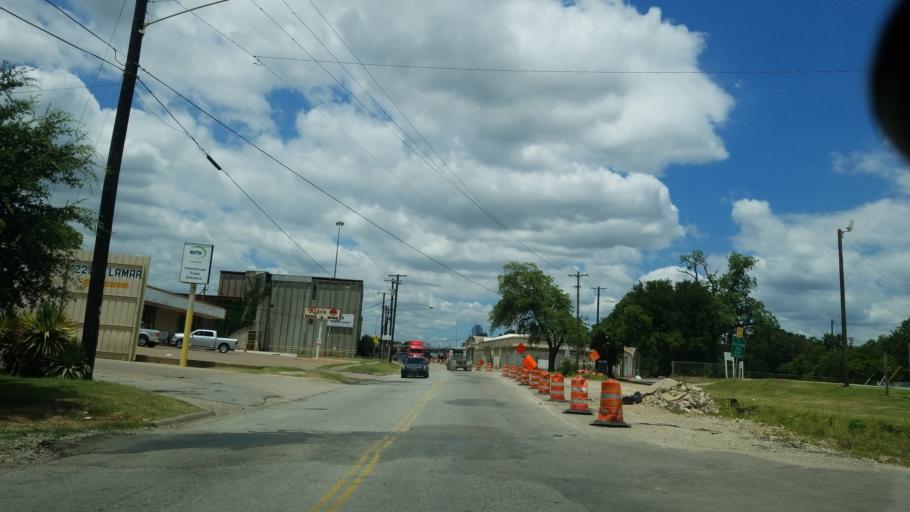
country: US
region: Texas
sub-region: Dallas County
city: Dallas
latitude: 32.7500
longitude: -96.7673
